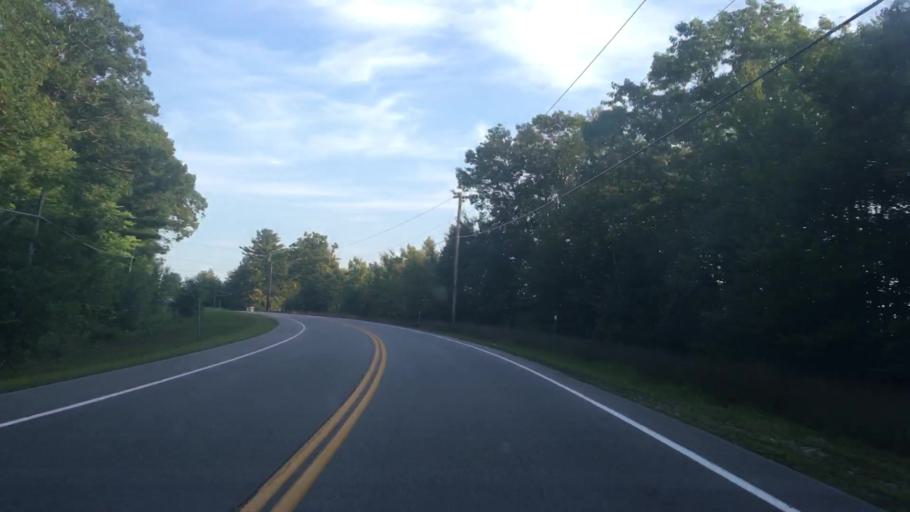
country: US
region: New Hampshire
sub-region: Belknap County
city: Gilmanton
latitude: 43.4405
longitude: -71.4191
